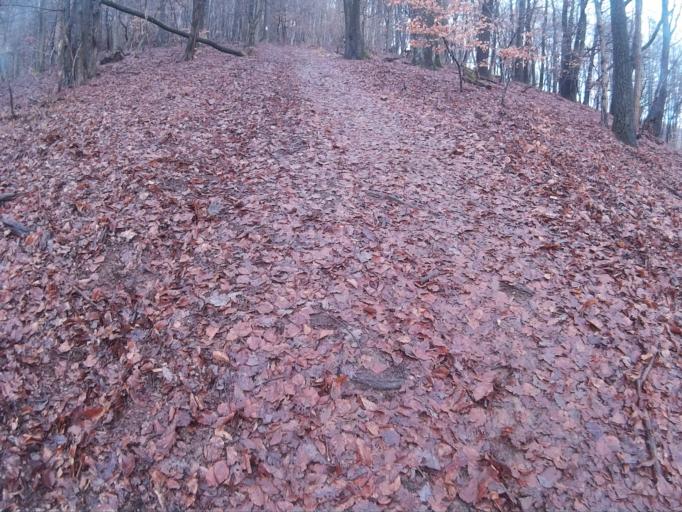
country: HU
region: Nograd
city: Somoskoujfalu
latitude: 48.1550
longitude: 19.7920
